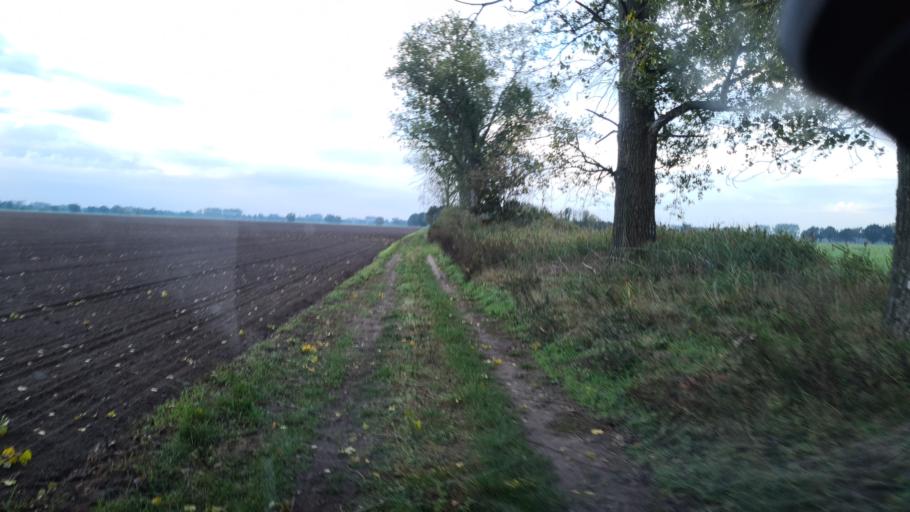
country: DE
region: Brandenburg
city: Schonewalde
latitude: 51.6882
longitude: 13.5696
